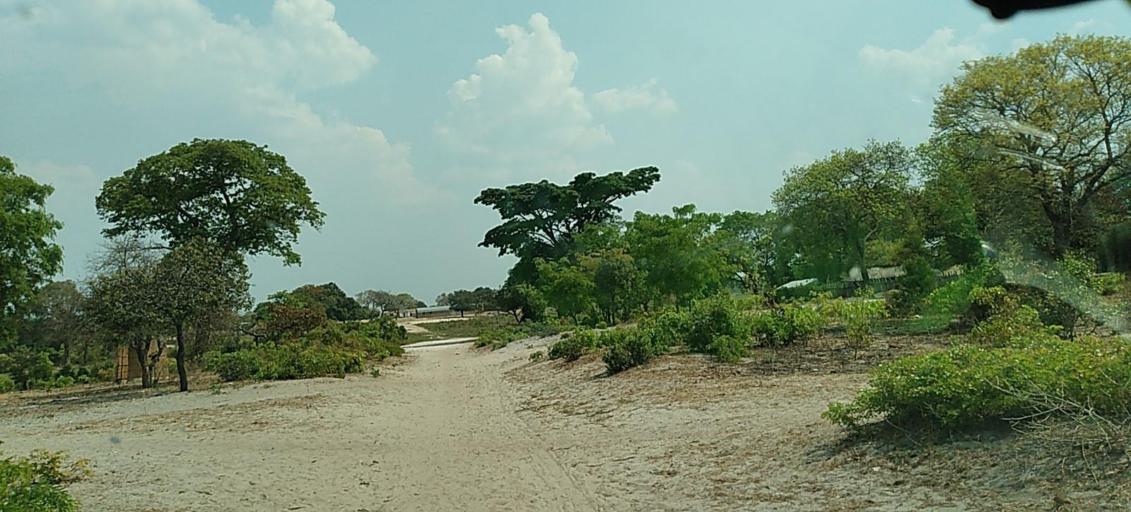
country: ZM
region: North-Western
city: Kabompo
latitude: -13.4465
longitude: 23.6676
